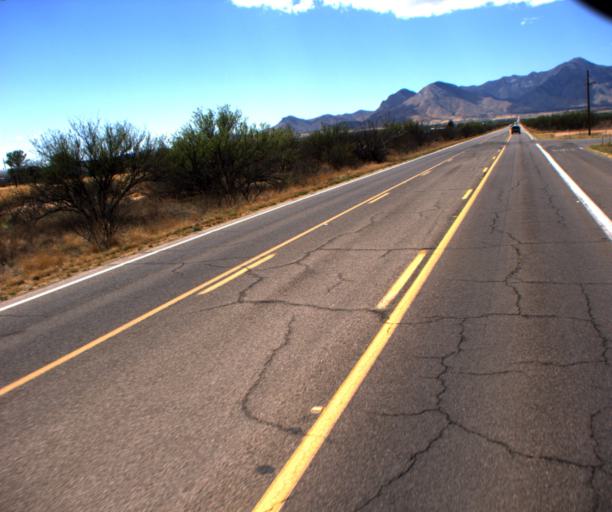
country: US
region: Arizona
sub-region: Cochise County
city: Sierra Vista Southeast
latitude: 31.3800
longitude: -110.1255
